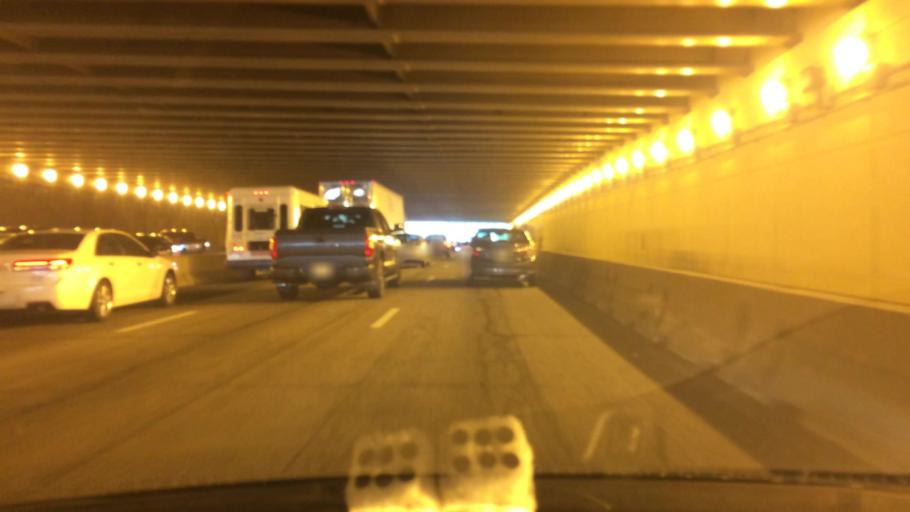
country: US
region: Pennsylvania
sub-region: Philadelphia County
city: Philadelphia
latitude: 39.9592
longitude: -75.1714
